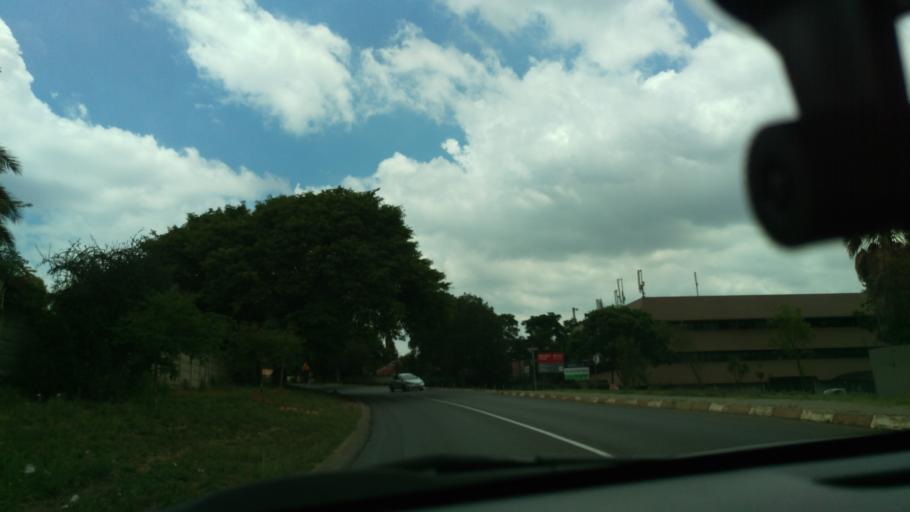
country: ZA
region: Gauteng
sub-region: City of Johannesburg Metropolitan Municipality
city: Midrand
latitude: -26.0477
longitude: 28.0525
